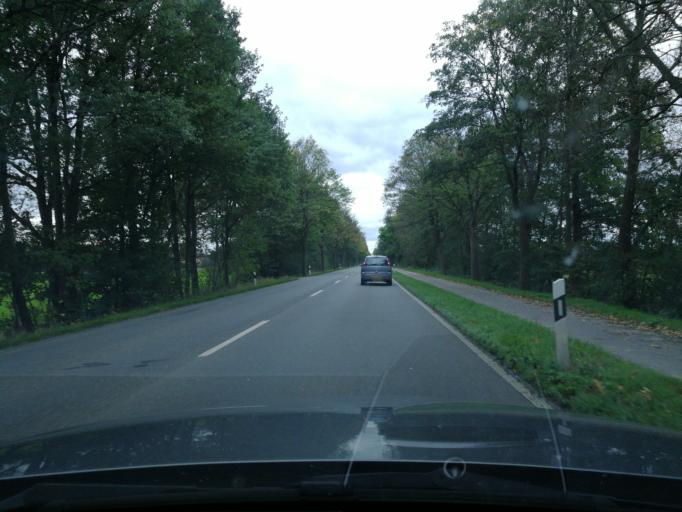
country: DE
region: North Rhine-Westphalia
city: Straelen
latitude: 51.4155
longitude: 6.2303
